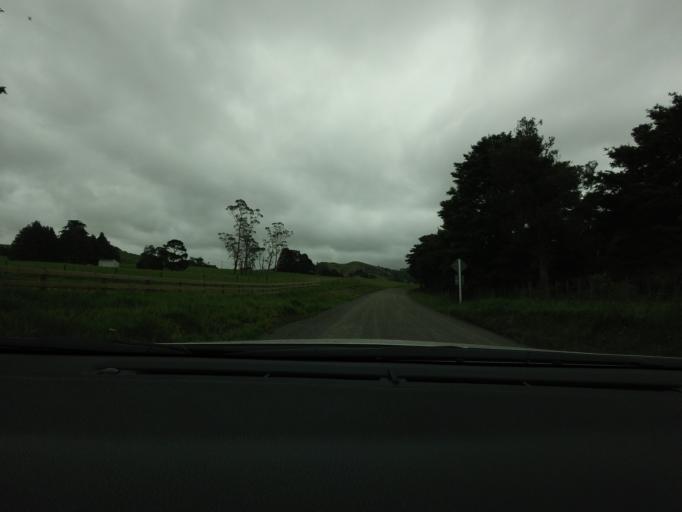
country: NZ
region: Auckland
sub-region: Auckland
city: Warkworth
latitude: -36.4788
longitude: 174.5844
